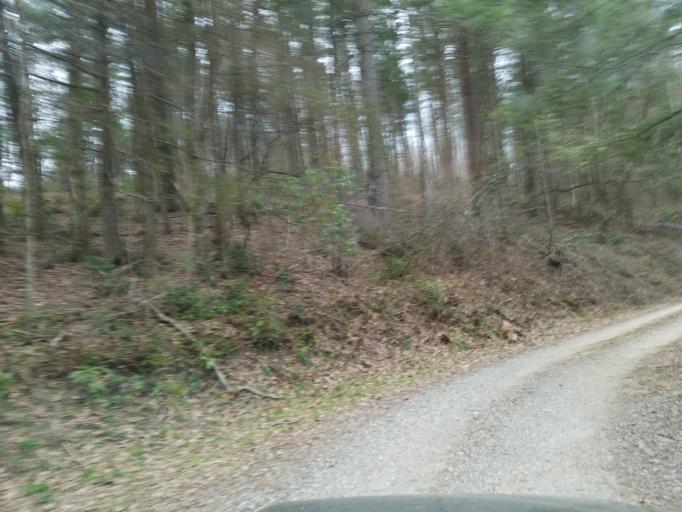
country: US
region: Georgia
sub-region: Union County
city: Blairsville
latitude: 34.7715
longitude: -84.0930
